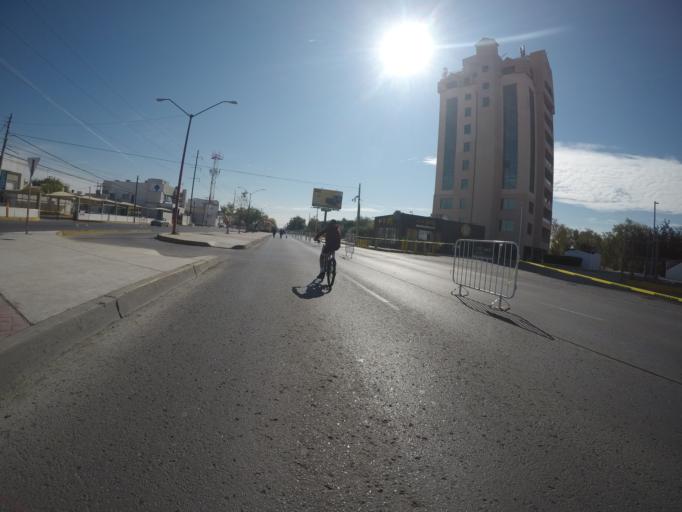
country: MX
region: Chihuahua
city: Ciudad Juarez
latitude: 31.7291
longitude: -106.4083
